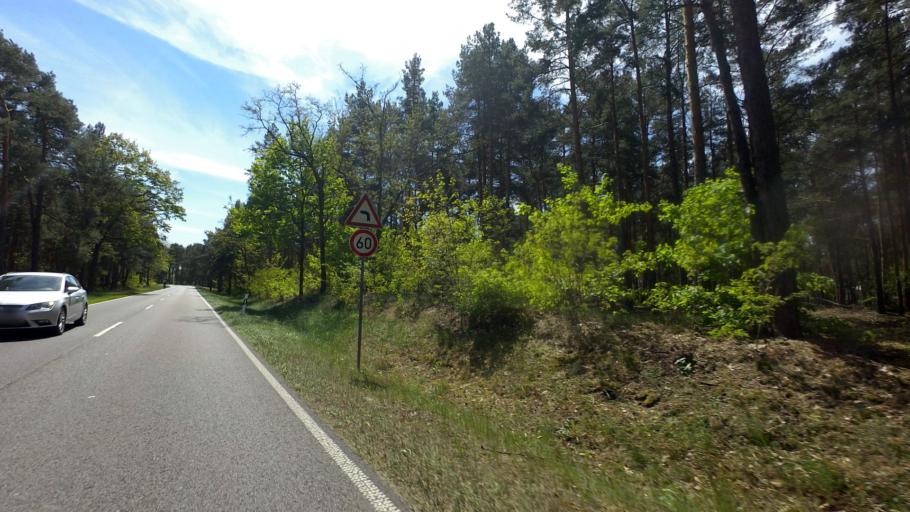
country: DE
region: Brandenburg
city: Luckenwalde
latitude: 52.1457
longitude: 13.1144
